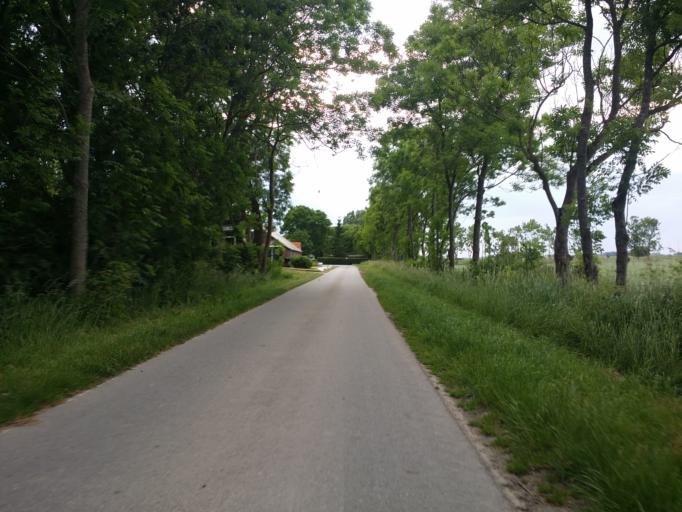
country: DE
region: Lower Saxony
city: Wittmund
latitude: 53.6421
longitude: 7.7857
